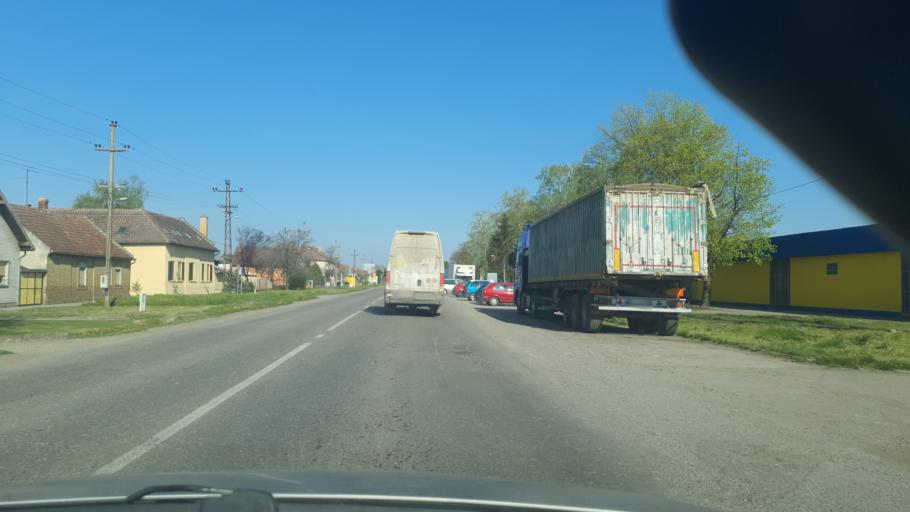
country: RS
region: Autonomna Pokrajina Vojvodina
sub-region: Zapadnobacki Okrug
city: Kula
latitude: 45.6633
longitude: 19.4459
